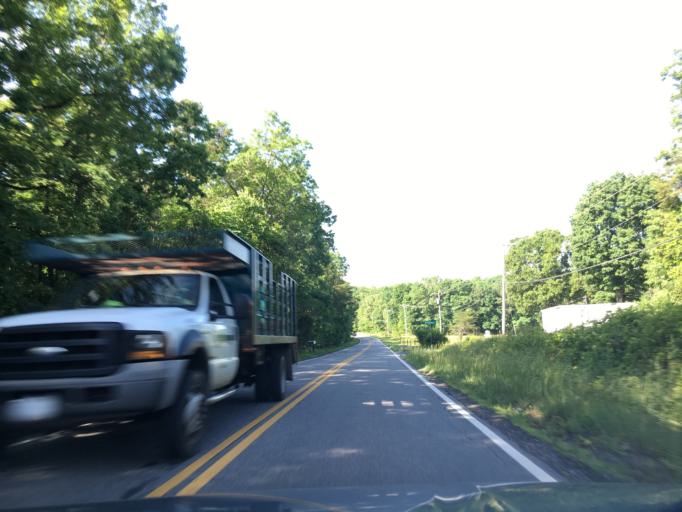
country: US
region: Virginia
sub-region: Campbell County
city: Rustburg
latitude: 37.3209
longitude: -79.1532
